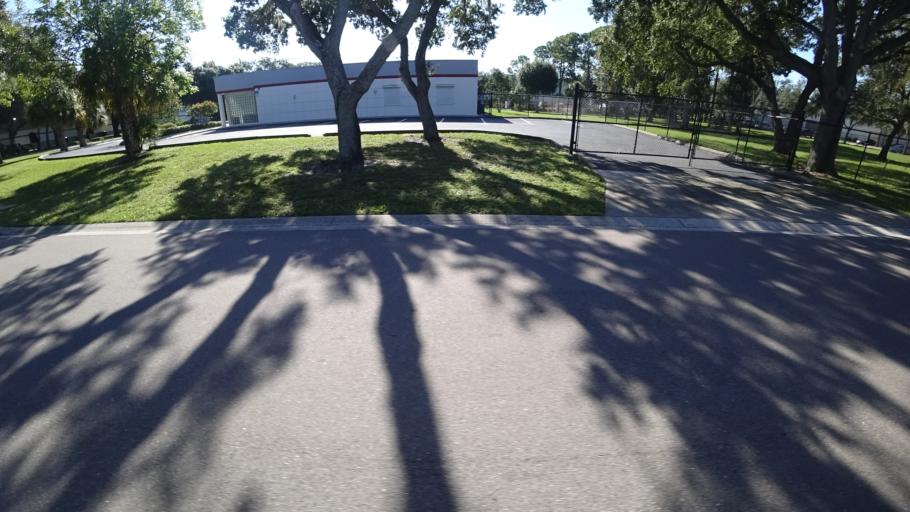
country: US
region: Florida
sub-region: Manatee County
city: Whitfield
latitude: 27.4268
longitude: -82.5368
